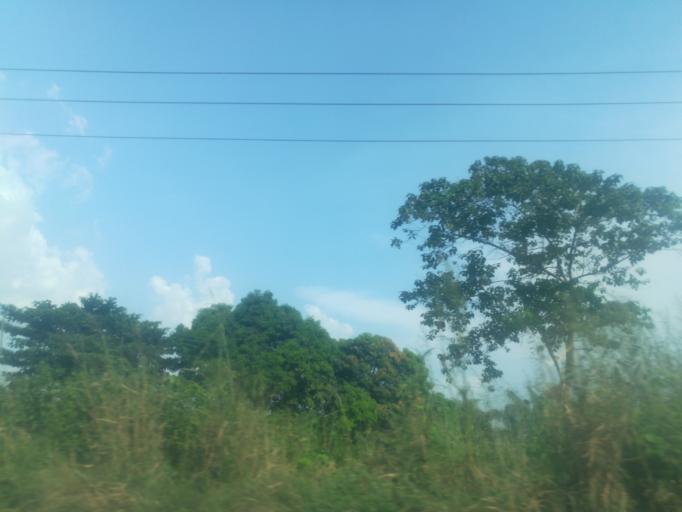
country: NG
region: Ogun
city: Abeokuta
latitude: 7.1037
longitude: 3.2973
